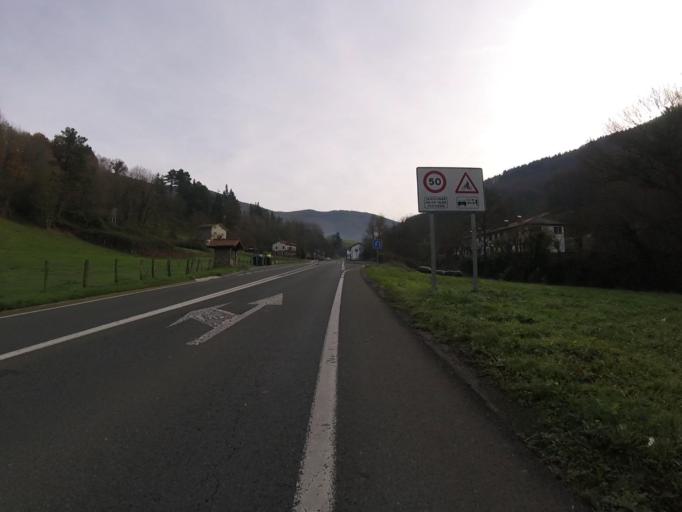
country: ES
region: Basque Country
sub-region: Provincia de Guipuzcoa
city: Berrobi
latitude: 43.1432
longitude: -2.0174
